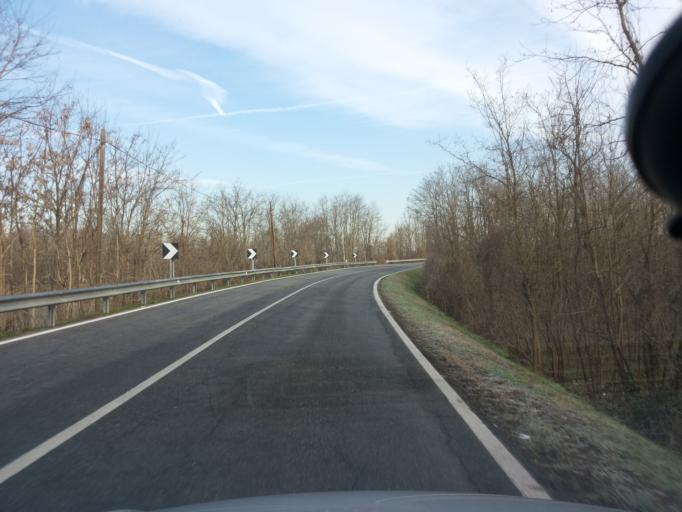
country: IT
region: Piedmont
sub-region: Provincia di Vercelli
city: Quinto Vercellese
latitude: 45.3797
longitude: 8.3725
